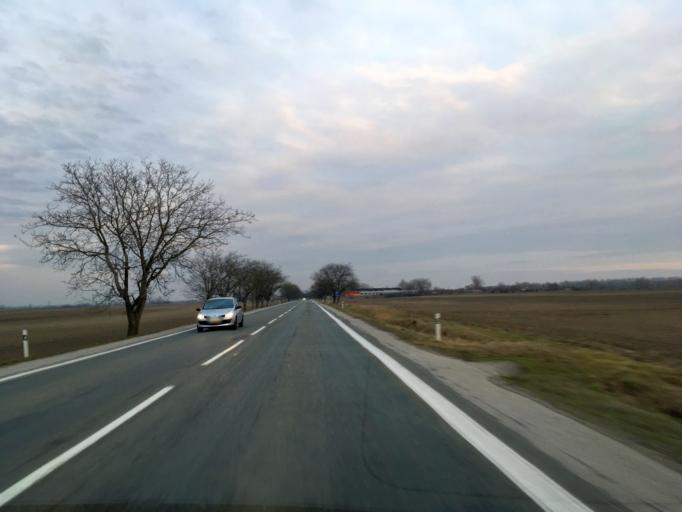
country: HU
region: Komarom-Esztergom
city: Acs
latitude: 47.7666
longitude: 18.0043
